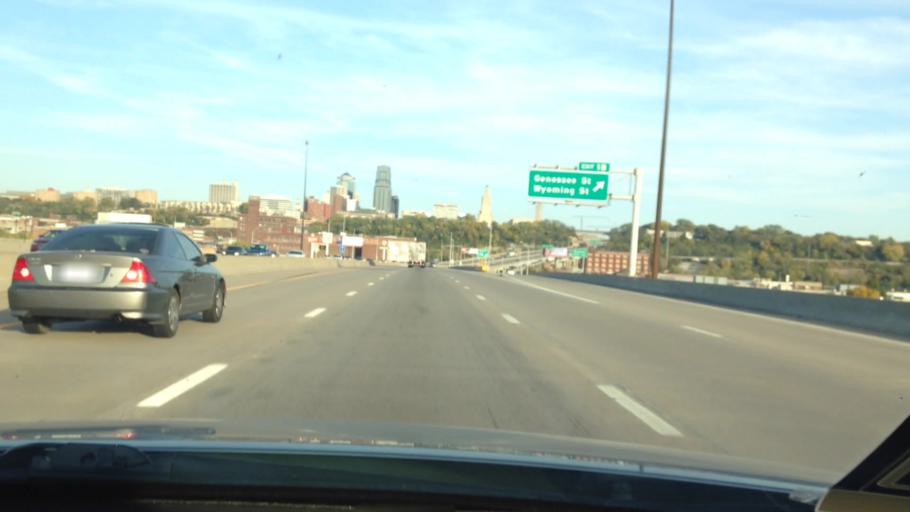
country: US
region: Kansas
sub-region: Wyandotte County
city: Kansas City
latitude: 39.0987
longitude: -94.6101
